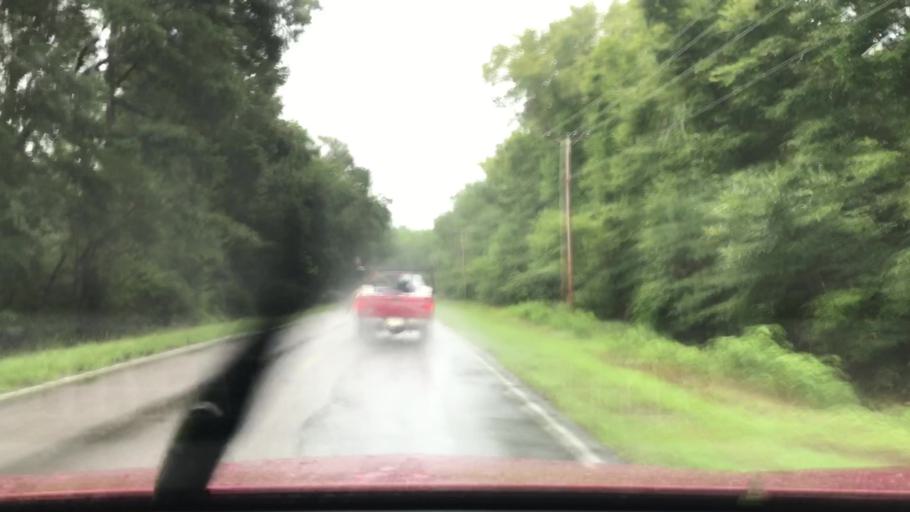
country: US
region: South Carolina
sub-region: Horry County
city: Conway
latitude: 33.8391
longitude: -79.0363
